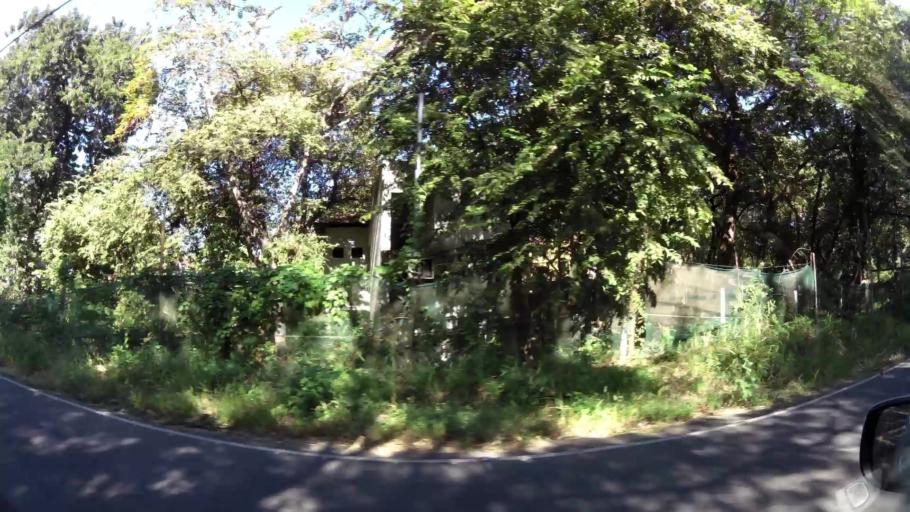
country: CR
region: Guanacaste
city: Sardinal
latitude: 10.4403
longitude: -85.7754
